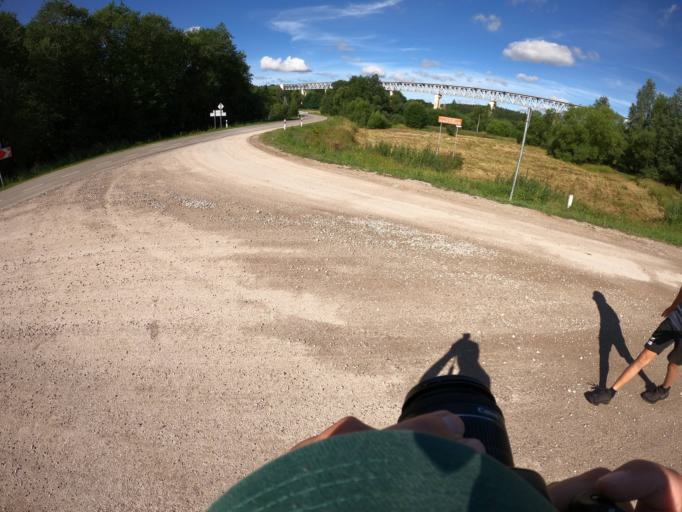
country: LT
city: Raseiniai
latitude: 55.5053
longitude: 23.0924
